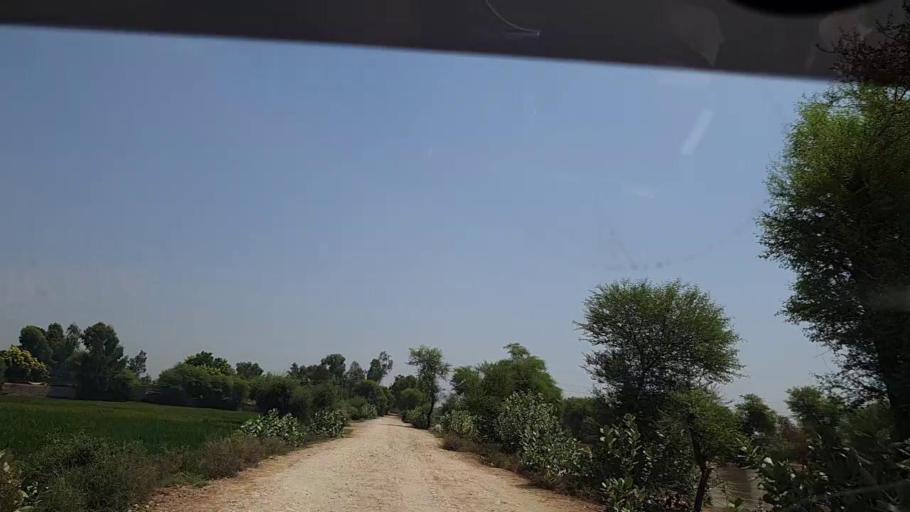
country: PK
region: Sindh
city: Ghauspur
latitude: 28.1682
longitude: 69.1235
